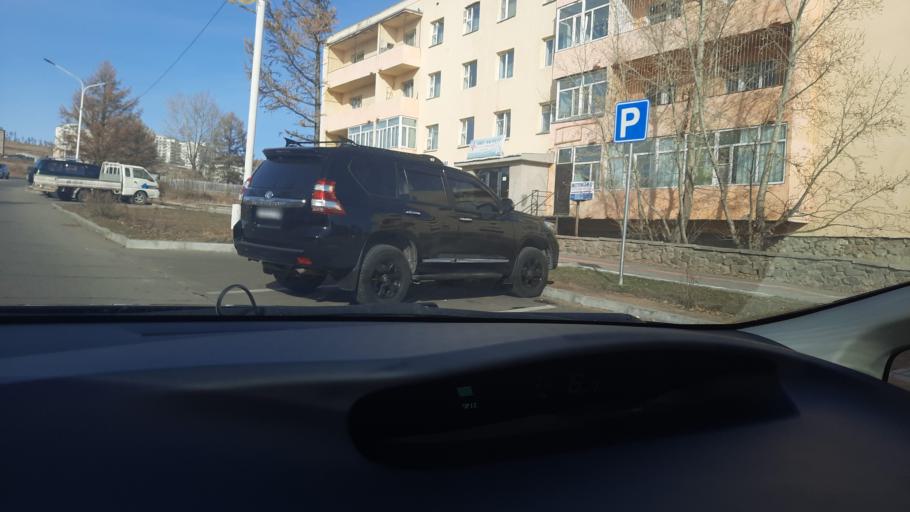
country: MN
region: Orhon
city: Erdenet
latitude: 49.0342
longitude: 104.0521
